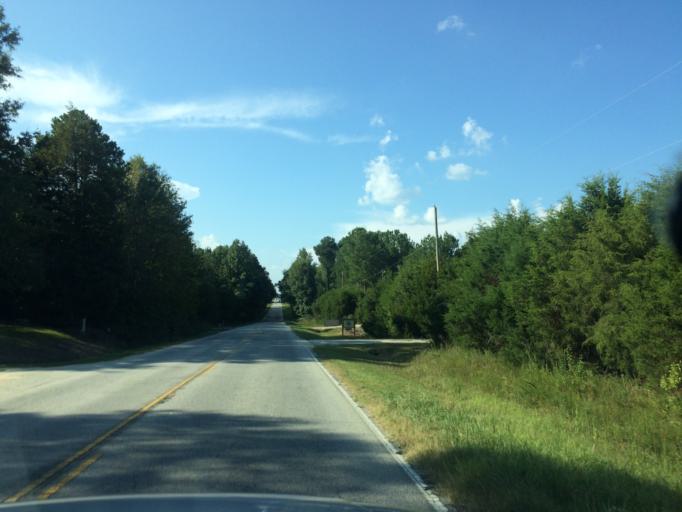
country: US
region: South Carolina
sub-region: Laurens County
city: Laurens
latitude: 34.5603
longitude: -82.0803
